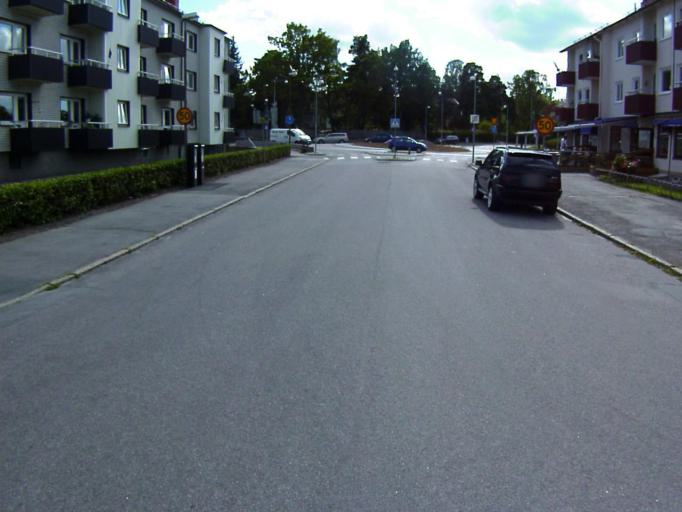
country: SE
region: Soedermanland
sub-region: Eskilstuna Kommun
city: Eskilstuna
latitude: 59.3748
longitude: 16.4878
